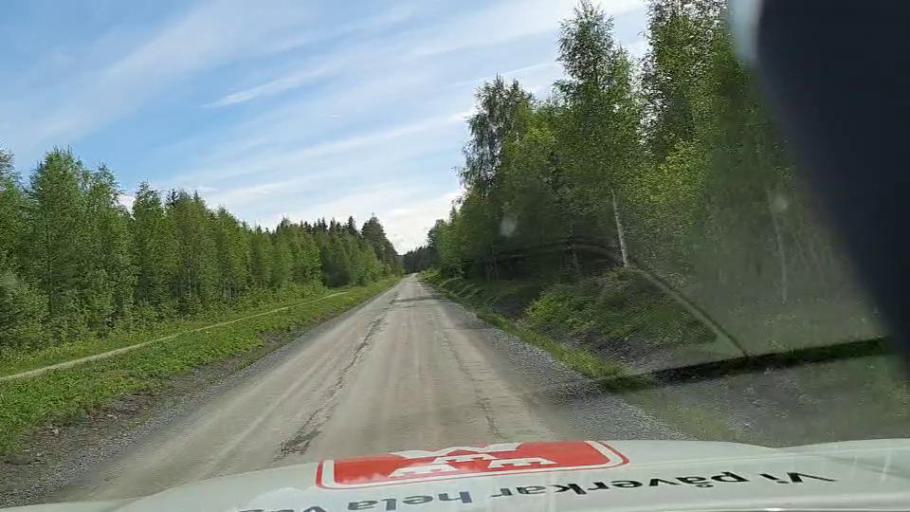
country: SE
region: Jaemtland
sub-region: OEstersunds Kommun
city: Brunflo
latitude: 62.9991
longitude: 14.8065
